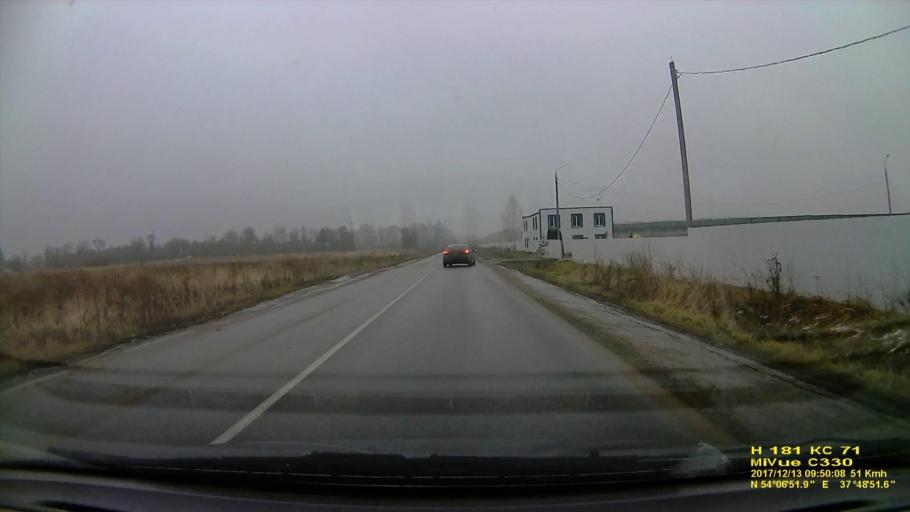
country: RU
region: Tula
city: Bolokhovo
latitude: 54.1144
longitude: 37.8144
